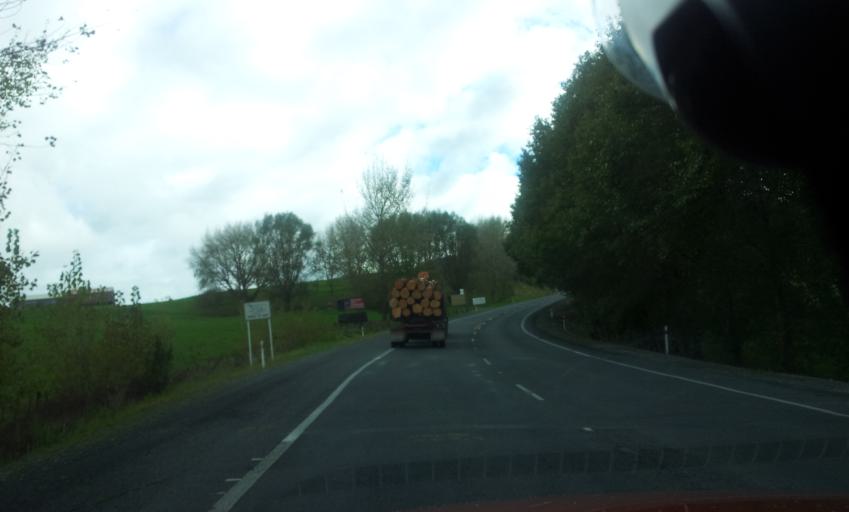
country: NZ
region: Auckland
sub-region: Auckland
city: Wellsford
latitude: -36.1076
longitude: 174.4333
